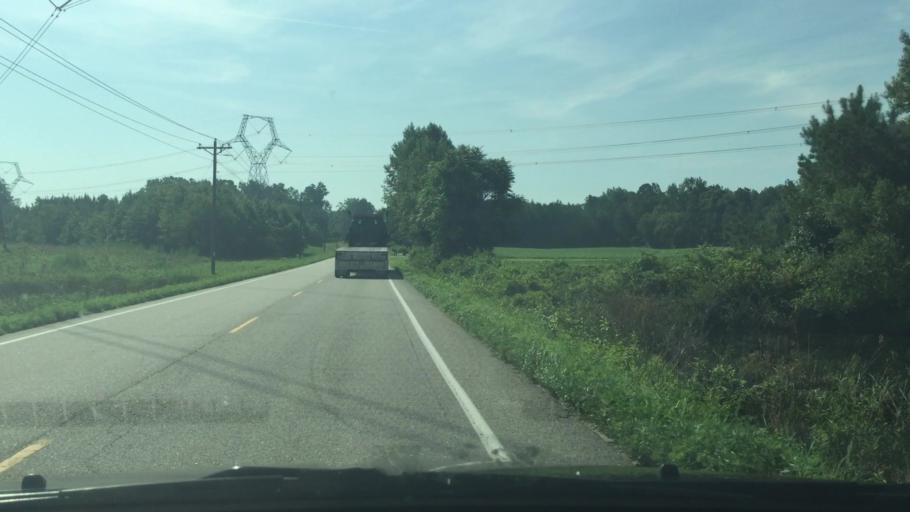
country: US
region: Virginia
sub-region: Sussex County
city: Sussex
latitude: 37.0598
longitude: -77.3293
